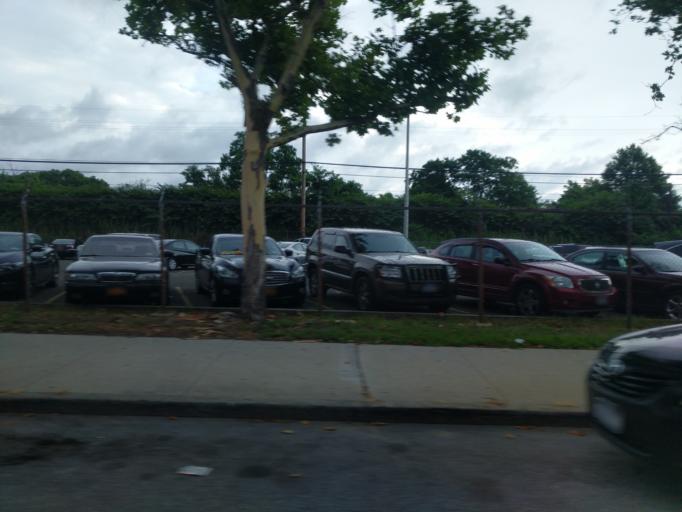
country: US
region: New York
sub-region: Queens County
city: Jamaica
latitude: 40.6756
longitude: -73.7668
